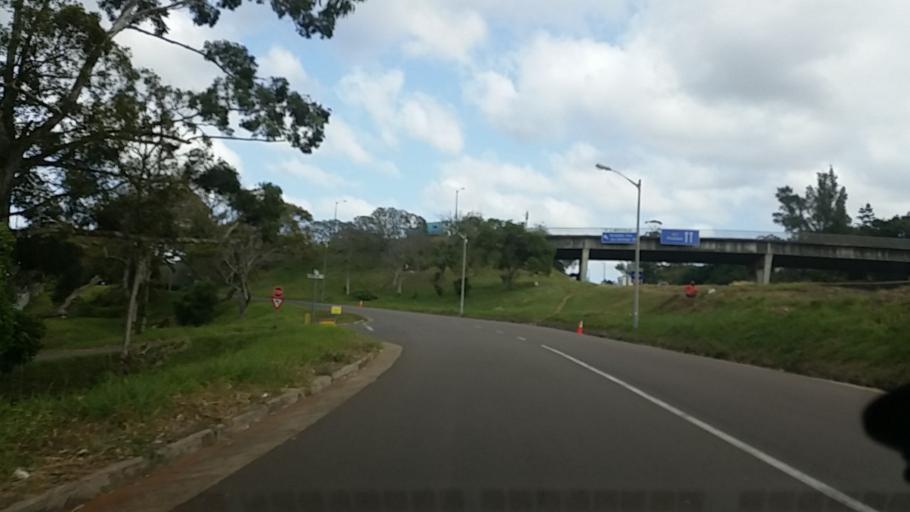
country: ZA
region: KwaZulu-Natal
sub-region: eThekwini Metropolitan Municipality
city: Berea
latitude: -29.8313
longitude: 30.9423
